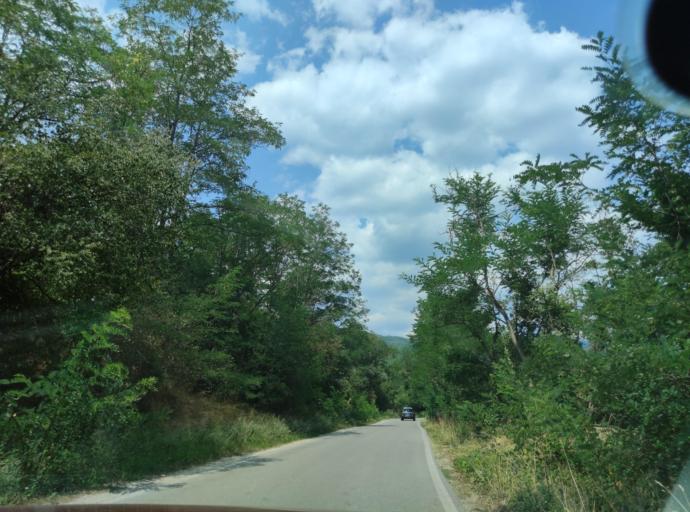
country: BG
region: Blagoevgrad
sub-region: Obshtina Belitsa
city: Belitsa
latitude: 41.9936
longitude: 23.5498
